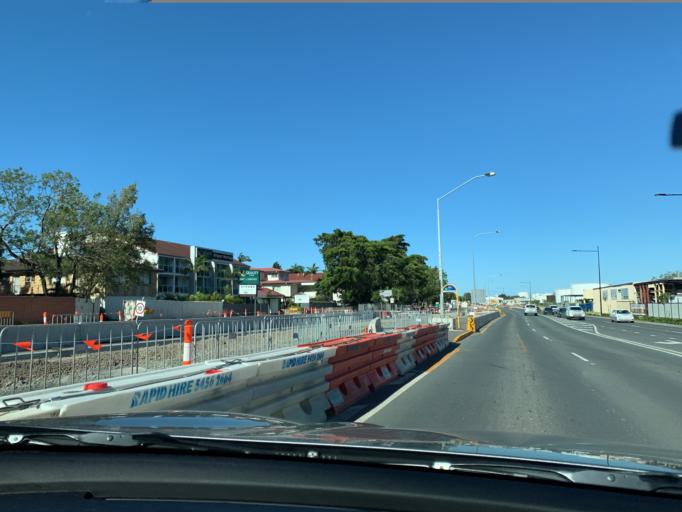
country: AU
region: Queensland
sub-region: Brisbane
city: Ascot
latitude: -27.4375
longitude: 153.0714
